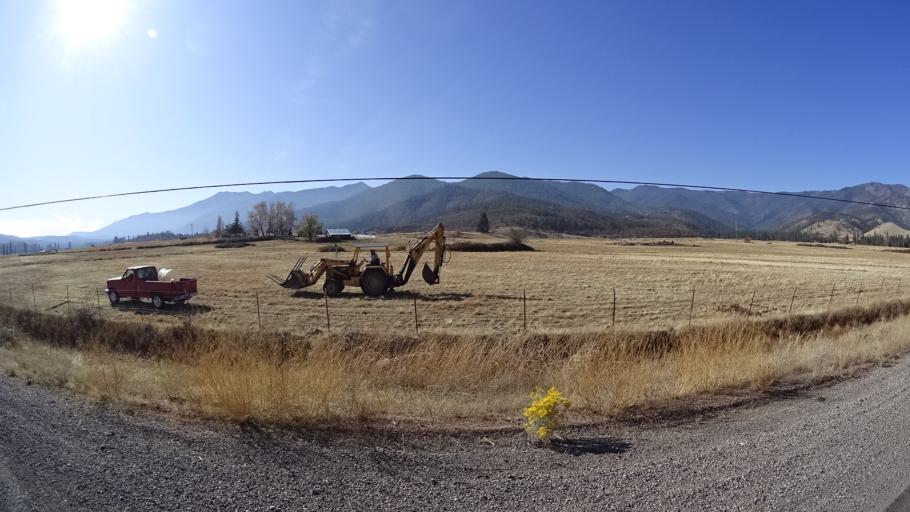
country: US
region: California
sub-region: Siskiyou County
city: Weed
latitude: 41.4431
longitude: -122.4402
